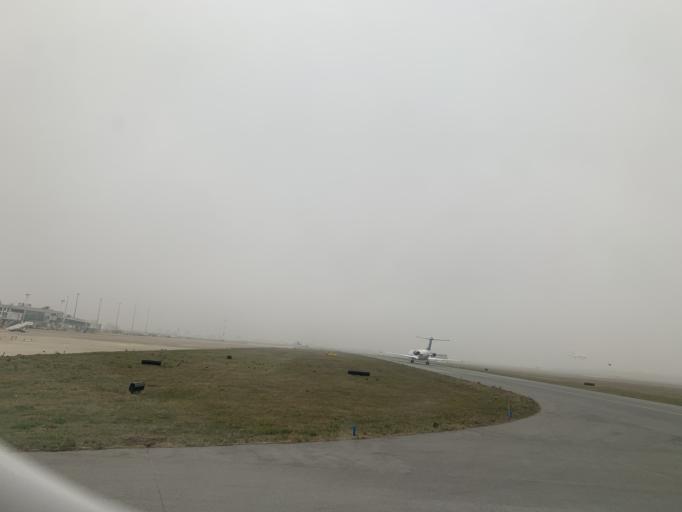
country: RS
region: Central Serbia
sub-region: Belgrade
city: Surcin
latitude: 44.8210
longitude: 20.2953
